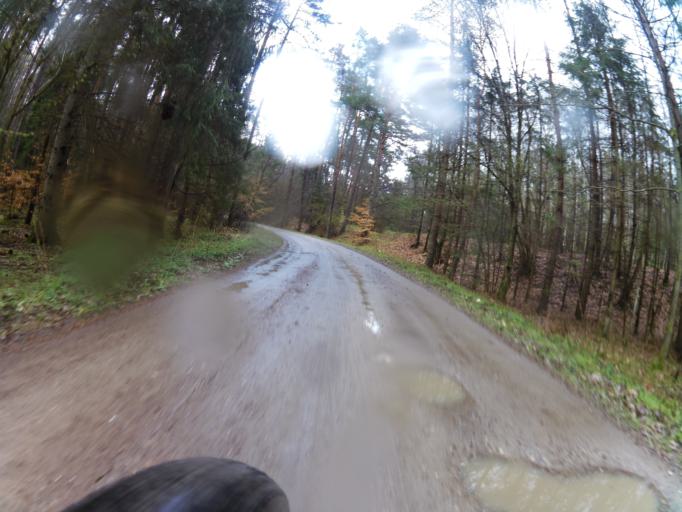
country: PL
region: Pomeranian Voivodeship
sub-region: Powiat slupski
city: Kepice
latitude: 54.2597
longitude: 16.7934
